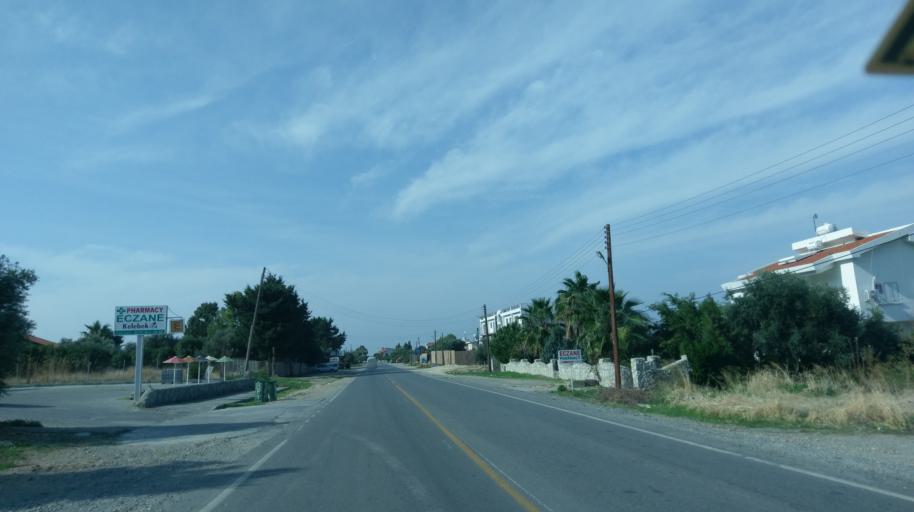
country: CY
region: Keryneia
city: Lapithos
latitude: 35.3496
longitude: 33.1501
